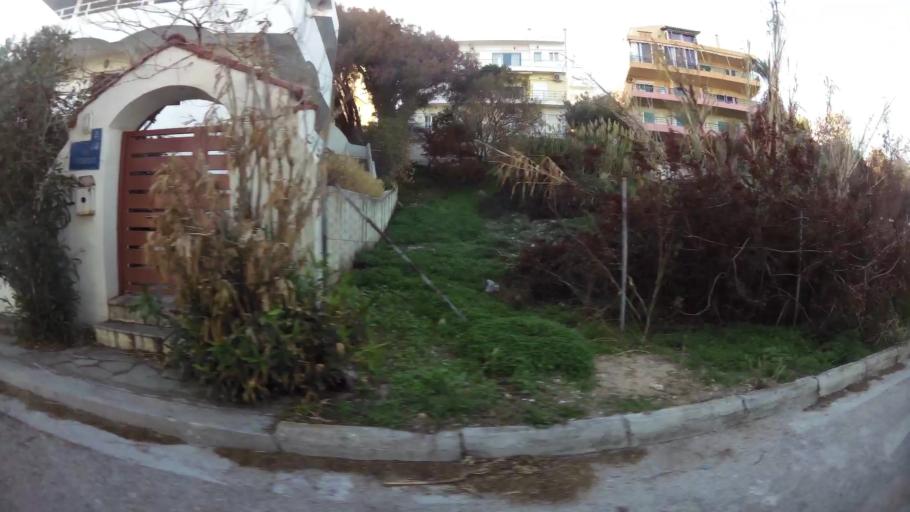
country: GR
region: Attica
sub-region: Nomarchia Anatolikis Attikis
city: Rafina
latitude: 38.0268
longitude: 24.0049
